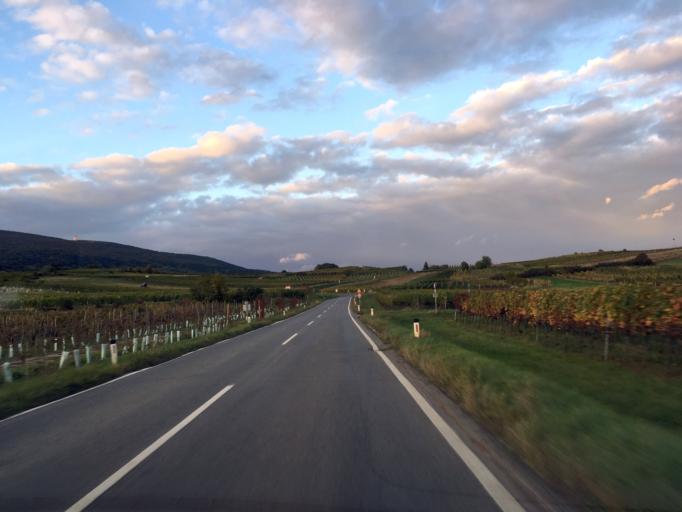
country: AT
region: Lower Austria
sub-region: Politischer Bezirk Baden
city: Pfaffstatten
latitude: 48.0225
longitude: 16.2582
